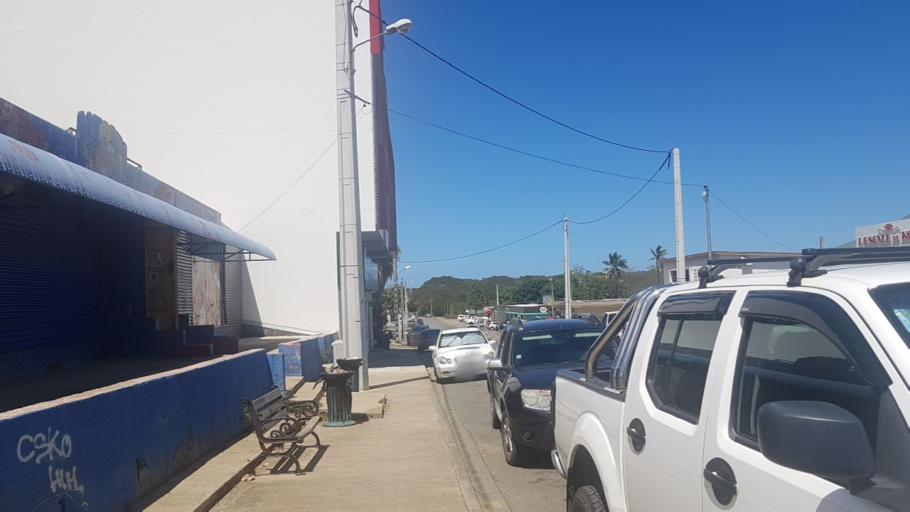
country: NC
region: North Province
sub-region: Kone
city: Kone
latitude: -21.0602
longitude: 164.8621
